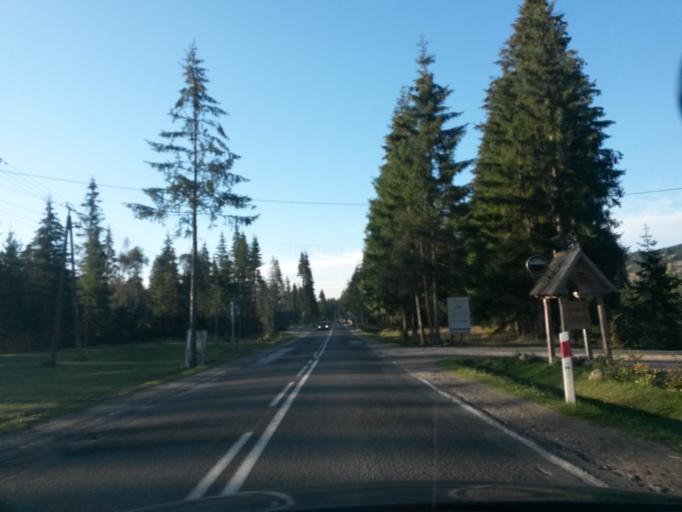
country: PL
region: Lesser Poland Voivodeship
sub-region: Powiat tatrzanski
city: Koscielisko
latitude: 49.2889
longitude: 19.8513
